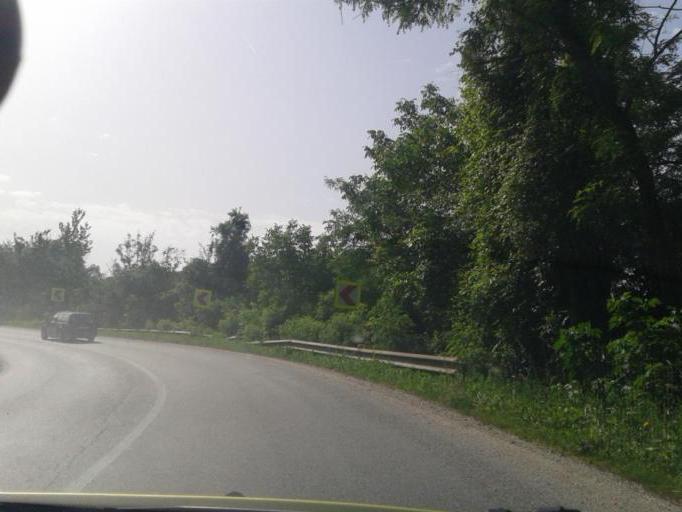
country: RO
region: Valcea
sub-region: Comuna Pietrari
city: Pietrari
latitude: 45.0977
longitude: 24.1268
